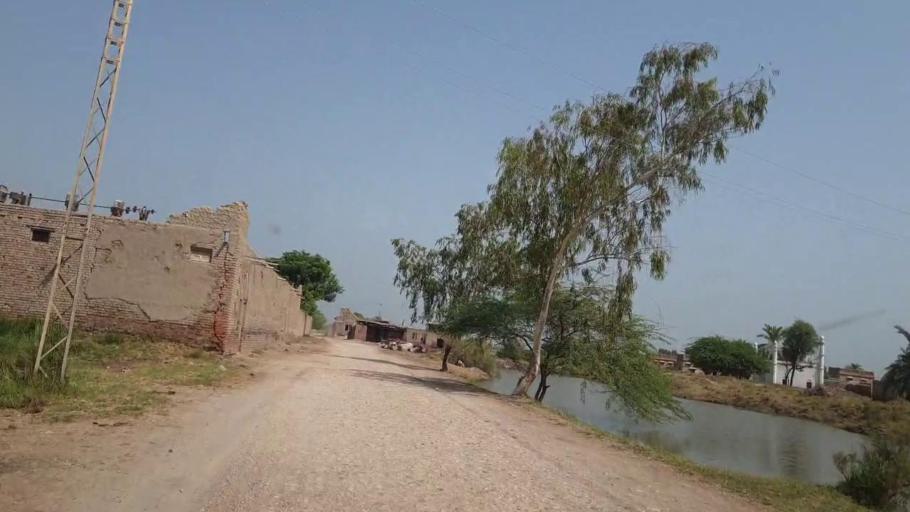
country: PK
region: Sindh
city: Lakhi
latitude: 27.8712
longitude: 68.6602
